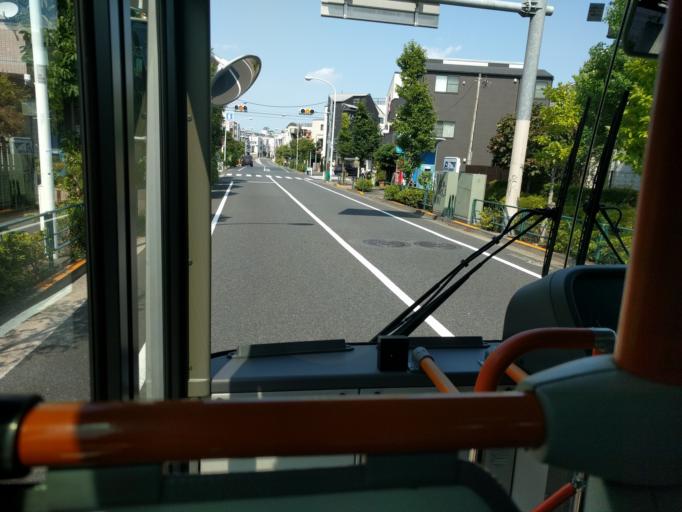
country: JP
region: Tokyo
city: Tokyo
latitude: 35.6175
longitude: 139.6405
